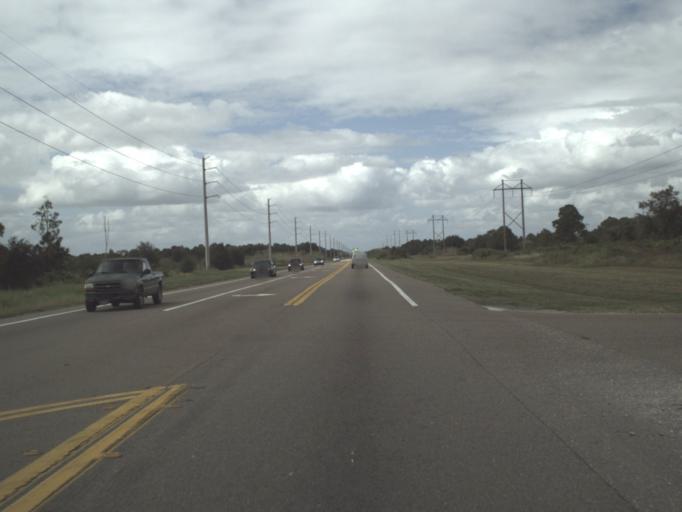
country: US
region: Florida
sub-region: Lee County
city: Gateway
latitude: 26.5752
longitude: -81.6986
